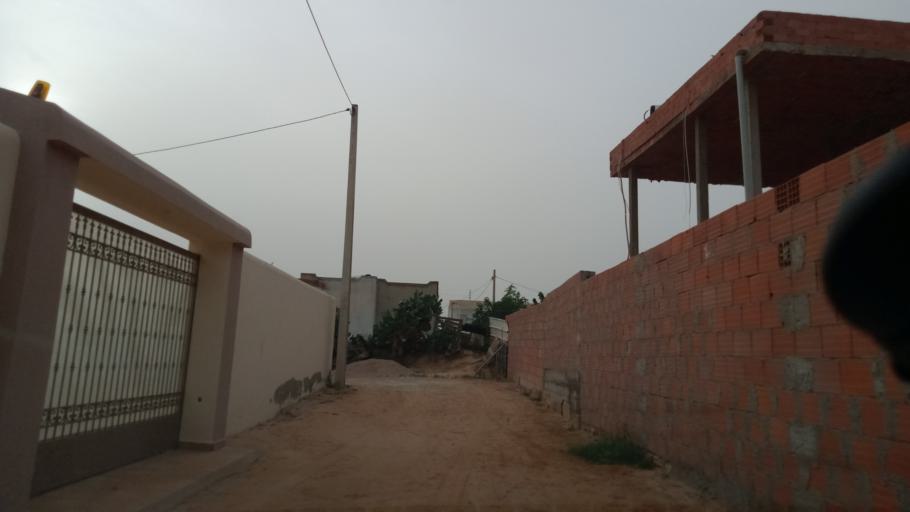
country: TN
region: Safaqis
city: Al Qarmadah
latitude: 34.7936
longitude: 10.7661
